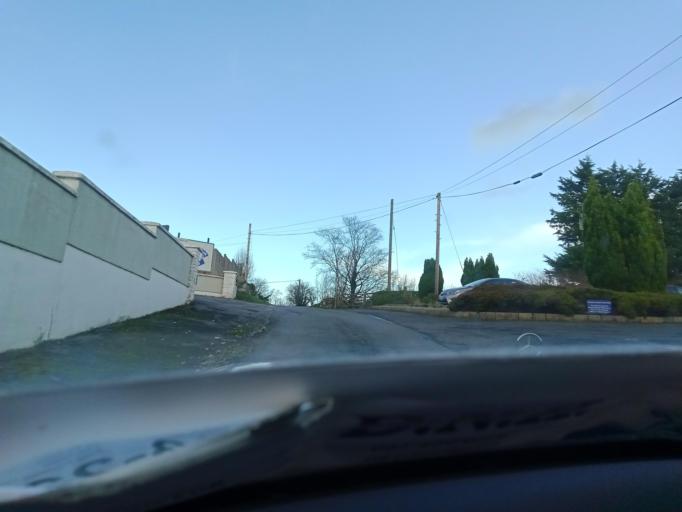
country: IE
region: Munster
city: Carrick-on-Suir
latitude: 52.3332
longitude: -7.4090
